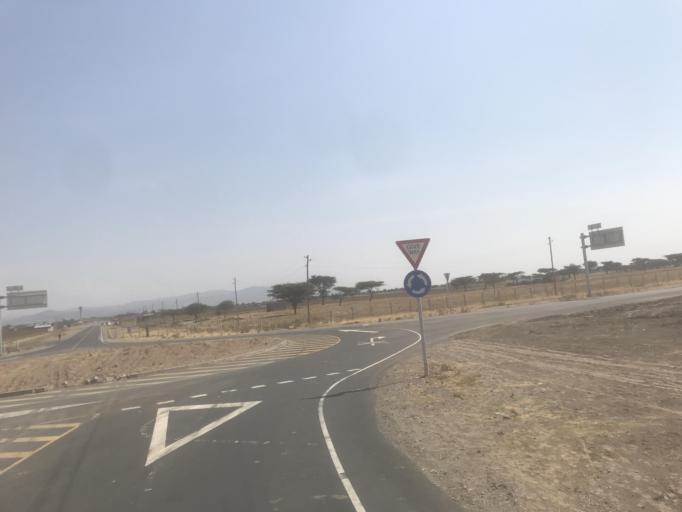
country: ET
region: Oromiya
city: Ziway
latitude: 7.9555
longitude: 38.6959
